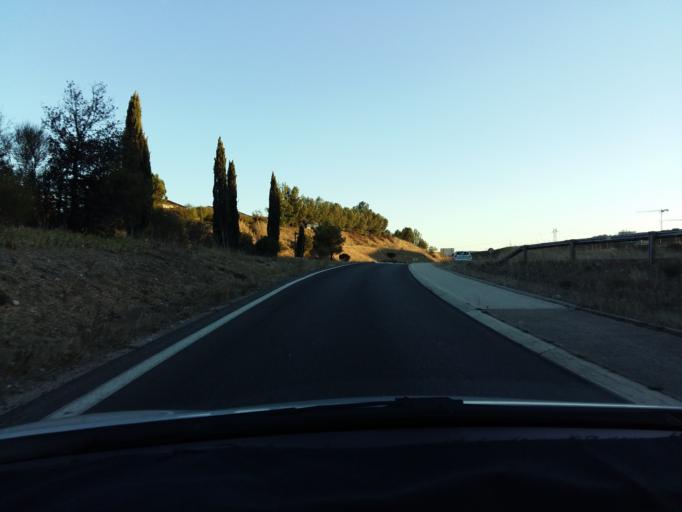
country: FR
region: Provence-Alpes-Cote d'Azur
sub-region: Departement des Bouches-du-Rhone
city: Cabries
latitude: 43.4946
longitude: 5.3505
